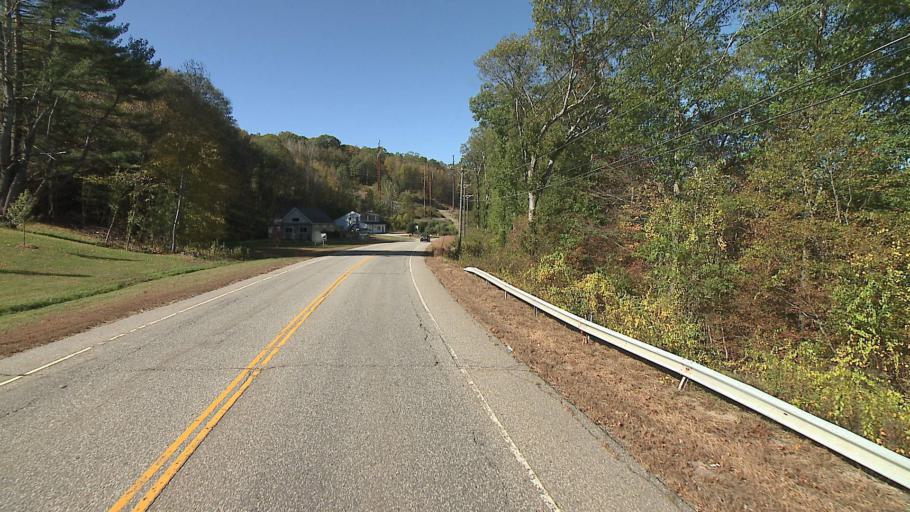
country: US
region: Connecticut
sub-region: Windham County
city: Willimantic
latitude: 41.7168
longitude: -72.2642
